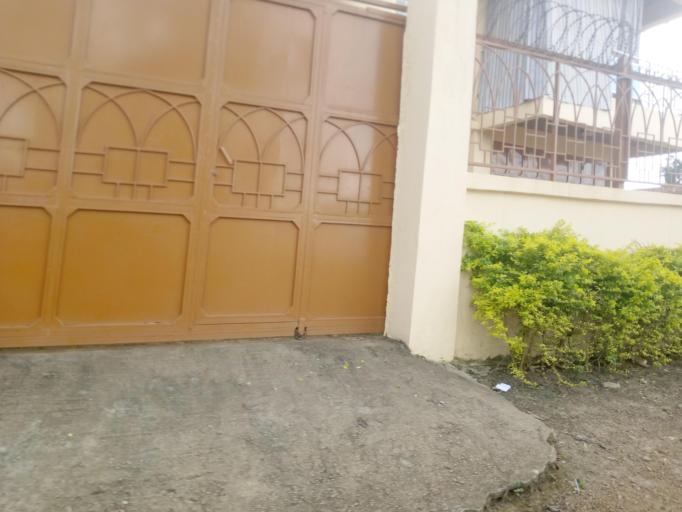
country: SL
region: Northern Province
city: Makeni
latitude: 8.8933
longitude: -12.0327
